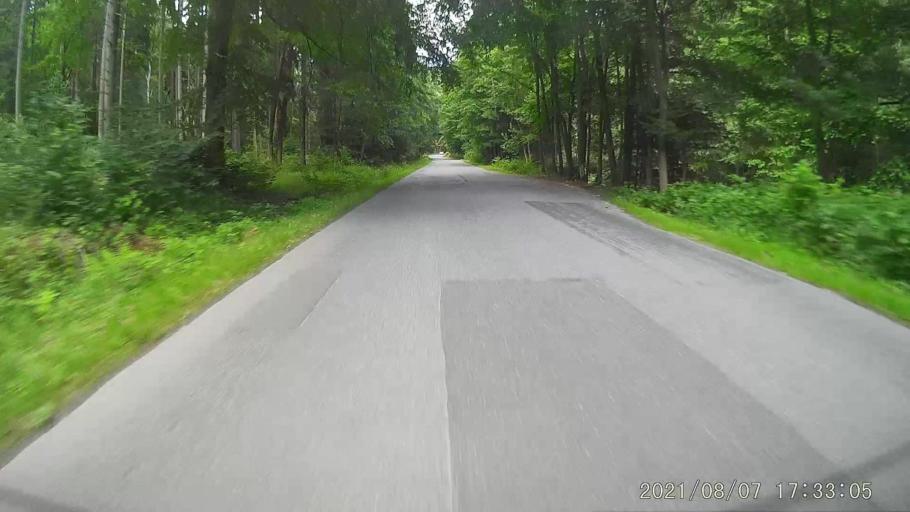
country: PL
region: Lower Silesian Voivodeship
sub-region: Powiat klodzki
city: Polanica-Zdroj
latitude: 50.3974
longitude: 16.4914
